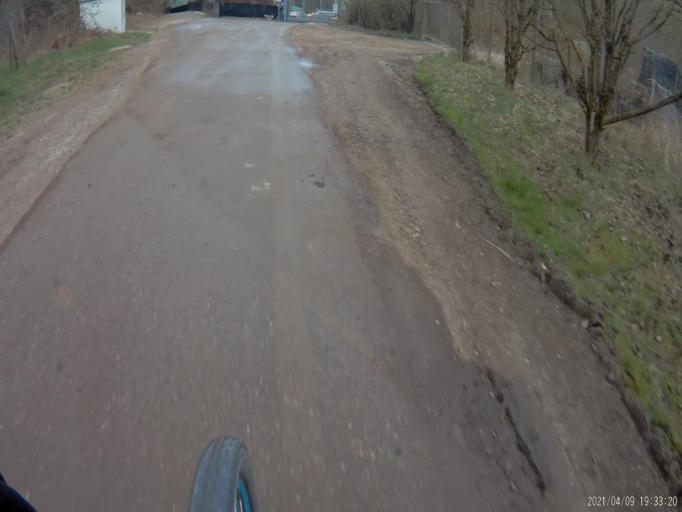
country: DE
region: Baden-Wuerttemberg
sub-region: Regierungsbezirk Stuttgart
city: Neuhausen auf den Fildern
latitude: 48.6803
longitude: 9.2992
